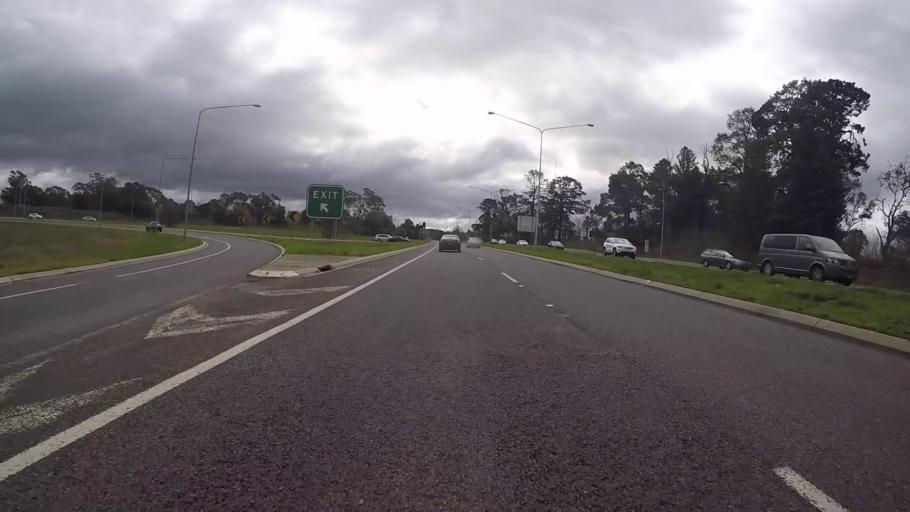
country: AU
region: Australian Capital Territory
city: Kaleen
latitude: -35.2246
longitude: 149.1219
